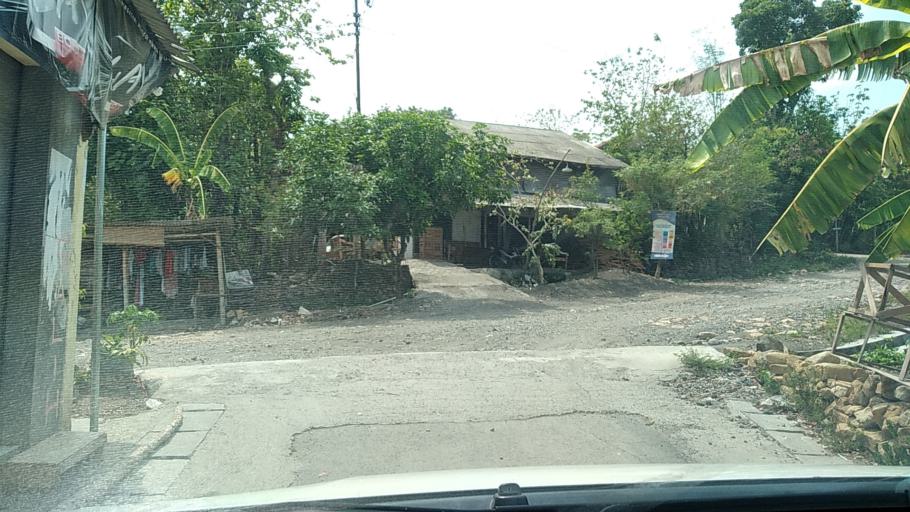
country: ID
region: Central Java
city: Mranggen
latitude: -7.0631
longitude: 110.4808
